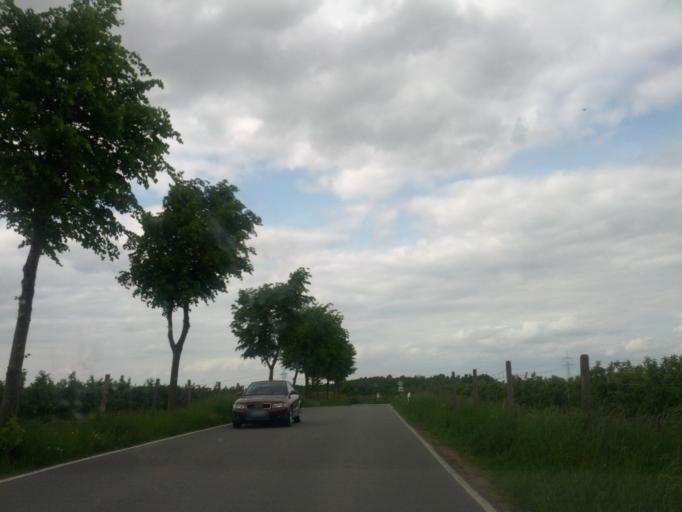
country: DE
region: Saxony
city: Kreischa
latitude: 50.9424
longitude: 13.7925
